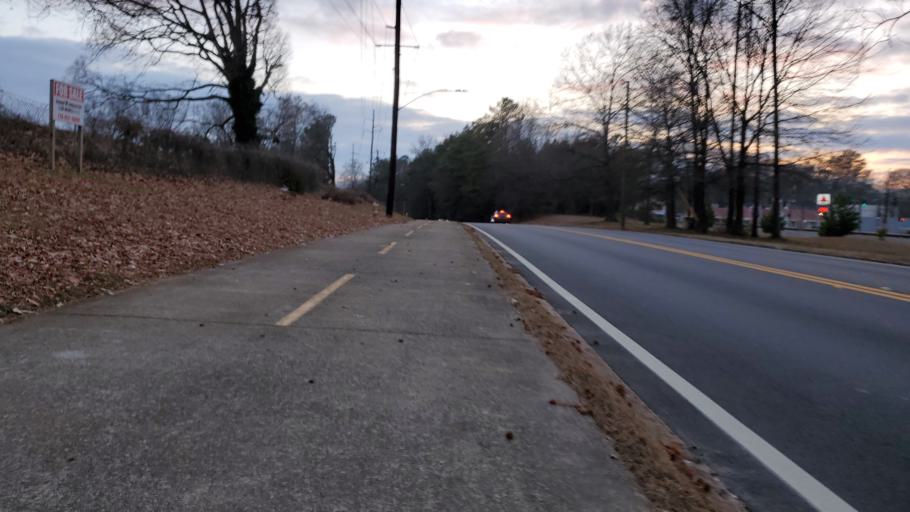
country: US
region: Georgia
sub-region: DeKalb County
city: Scottdale
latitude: 33.7954
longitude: -84.2616
